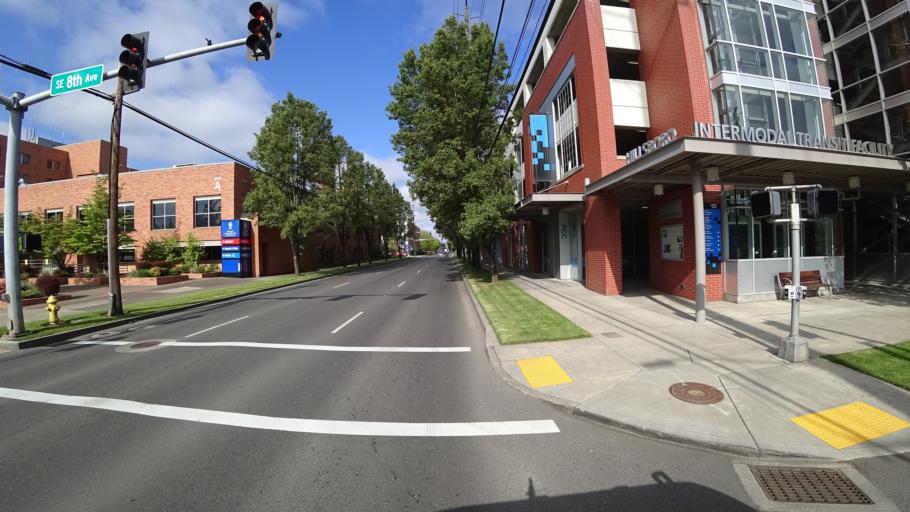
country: US
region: Oregon
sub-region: Washington County
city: Hillsboro
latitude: 45.5201
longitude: -122.9773
